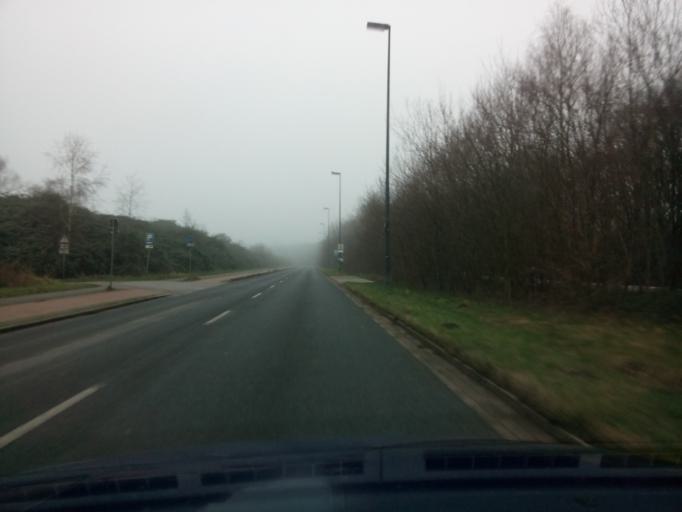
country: DE
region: Bremen
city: Bremen
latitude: 53.1150
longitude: 8.8385
